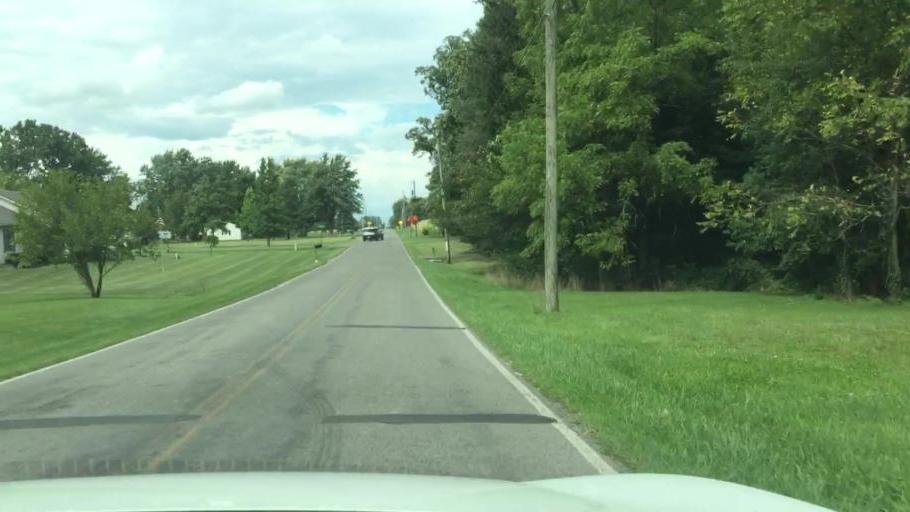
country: US
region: Ohio
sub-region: Champaign County
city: Urbana
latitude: 40.0950
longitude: -83.7137
